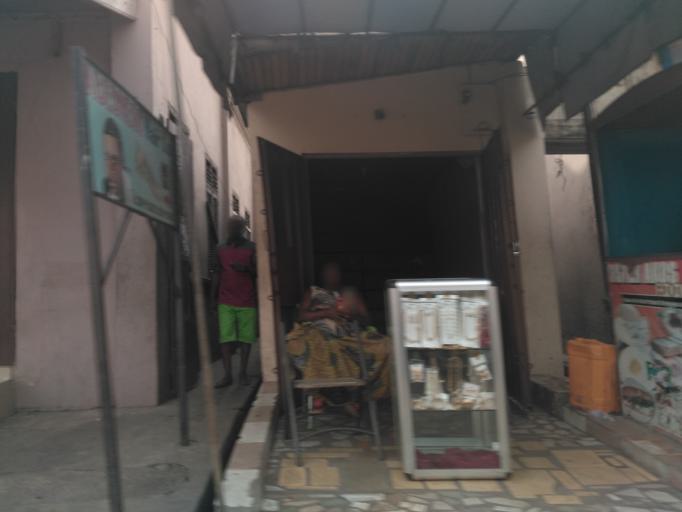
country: GH
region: Ashanti
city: Kumasi
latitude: 6.6886
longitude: -1.6106
